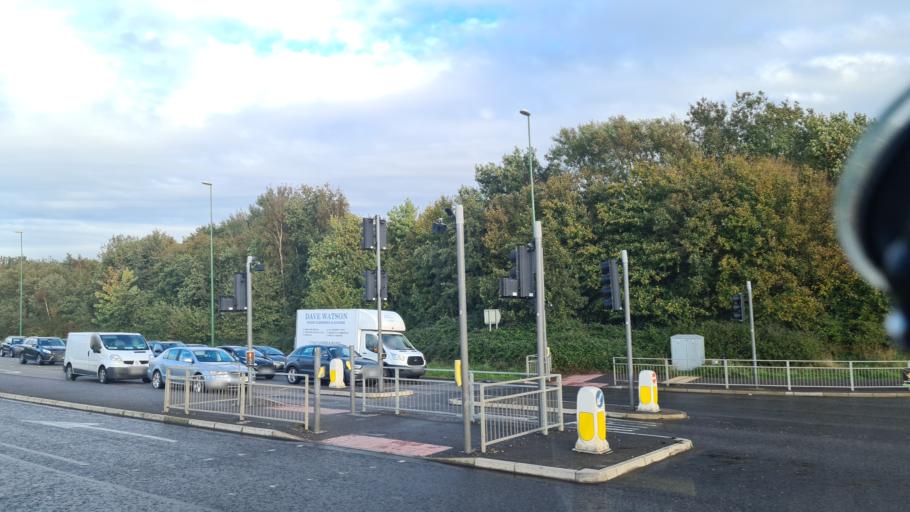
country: GB
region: England
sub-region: West Sussex
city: Littlehampton
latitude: 50.8201
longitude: -0.5577
